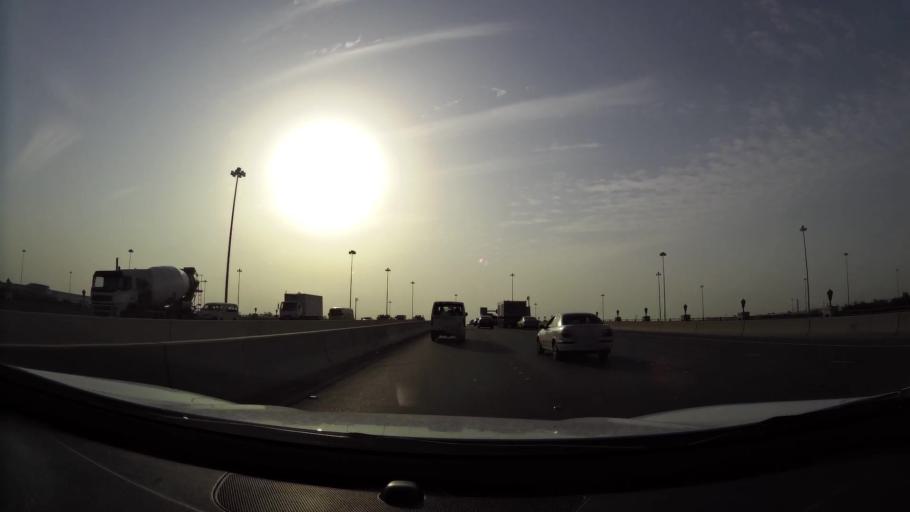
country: AE
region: Abu Dhabi
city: Abu Dhabi
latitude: 24.3469
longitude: 54.5271
